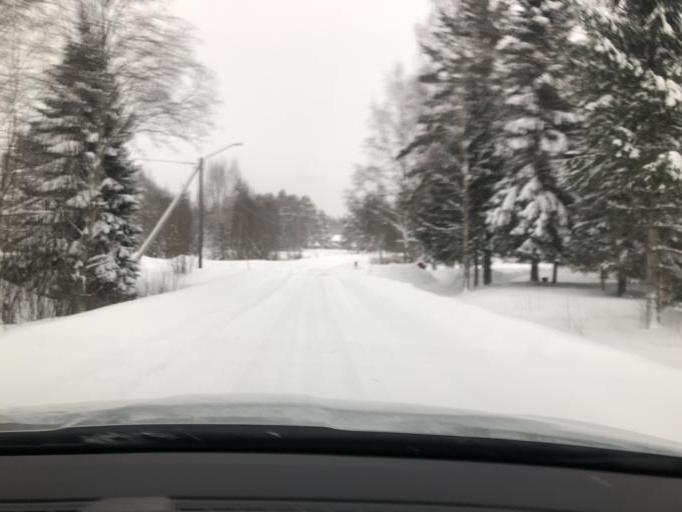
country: SE
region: Vaesterbotten
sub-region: Umea Kommun
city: Saevar
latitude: 63.9448
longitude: 20.7062
